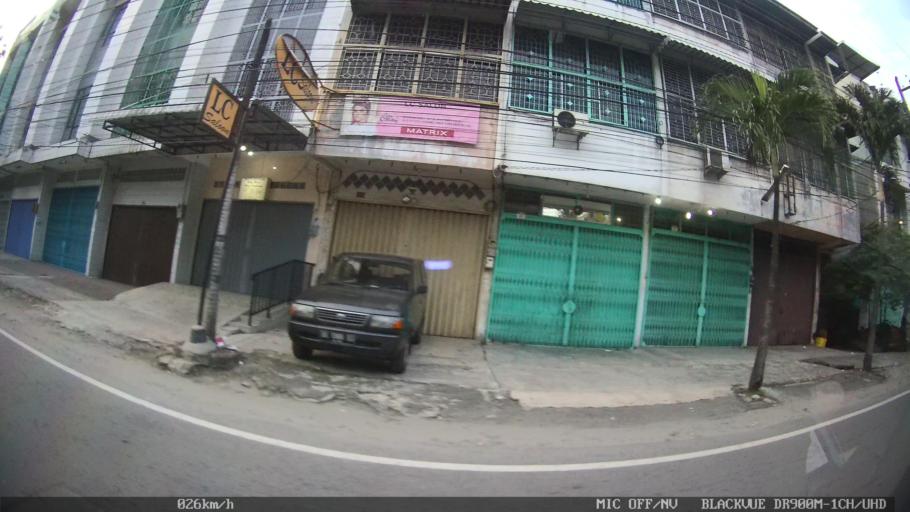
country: ID
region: North Sumatra
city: Medan
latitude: 3.5887
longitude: 98.6965
